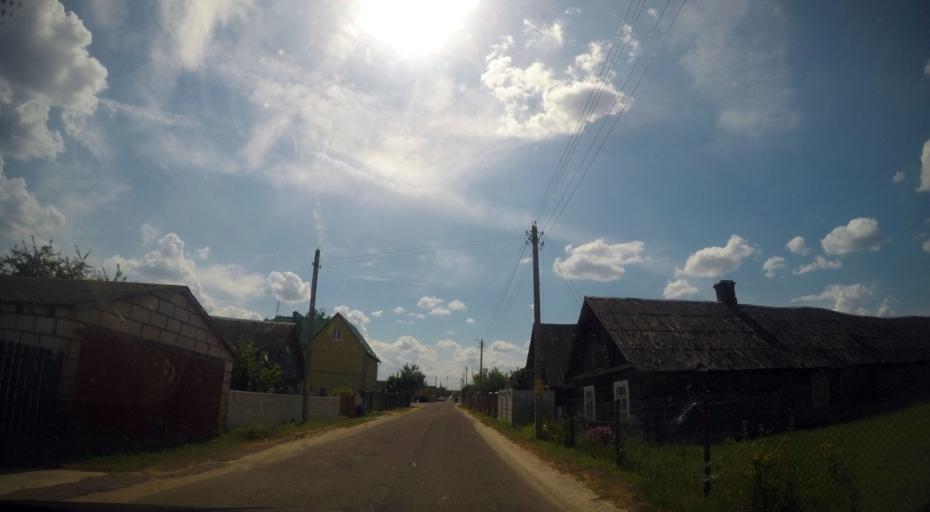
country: BY
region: Grodnenskaya
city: Hrodna
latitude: 53.6285
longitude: 23.8411
